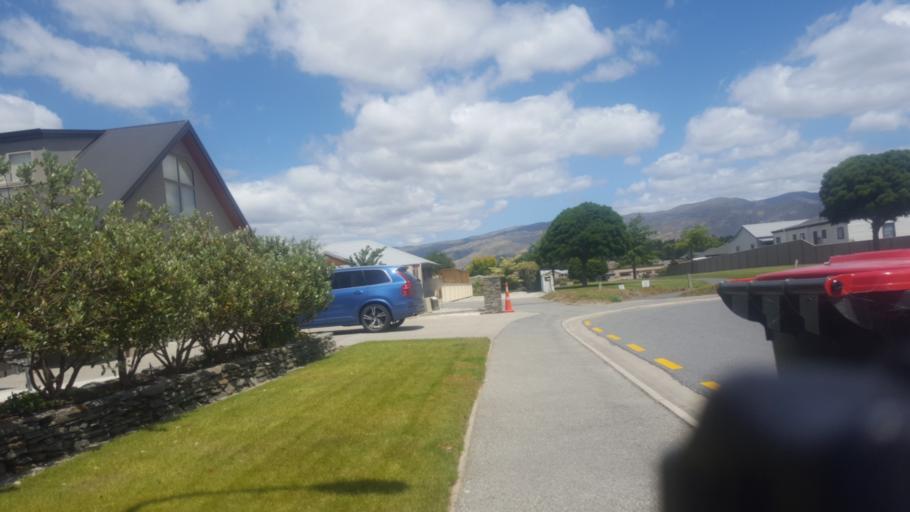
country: NZ
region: Otago
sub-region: Queenstown-Lakes District
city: Wanaka
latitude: -45.0504
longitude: 169.1981
